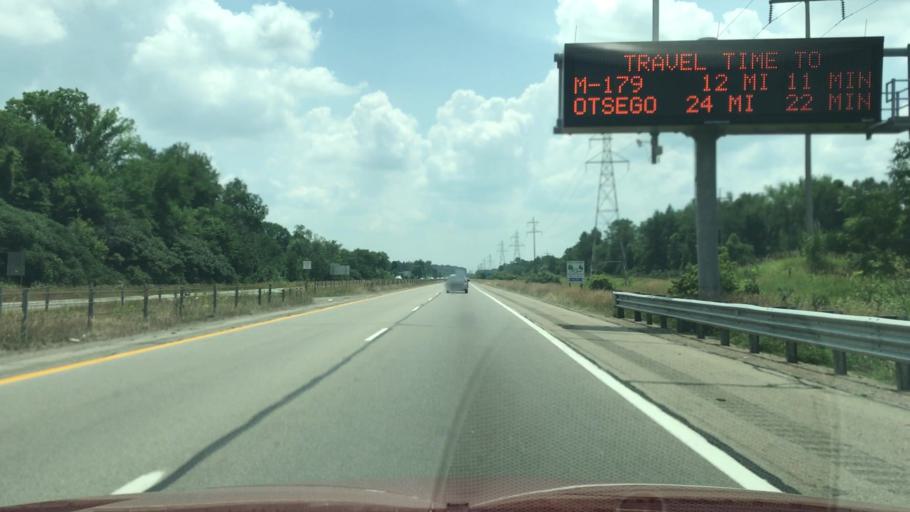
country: US
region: Michigan
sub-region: Kent County
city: Cutlerville
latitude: 42.7977
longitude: -85.6688
